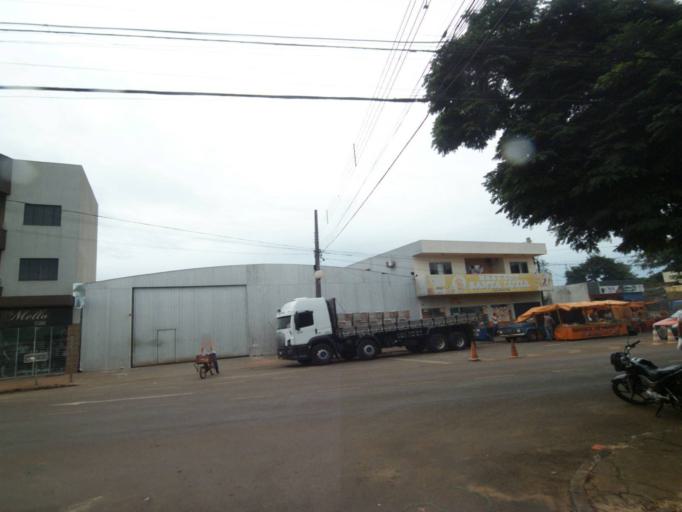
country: BR
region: Parana
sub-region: Campo Mourao
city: Campo Mourao
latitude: -24.0266
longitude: -52.3627
